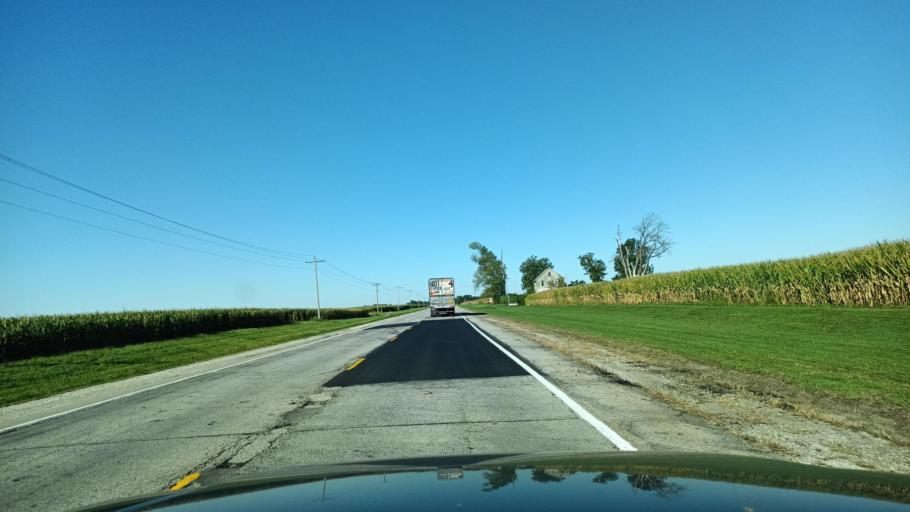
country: US
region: Illinois
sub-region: Warren County
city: Monmouth
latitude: 40.8783
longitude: -90.6919
